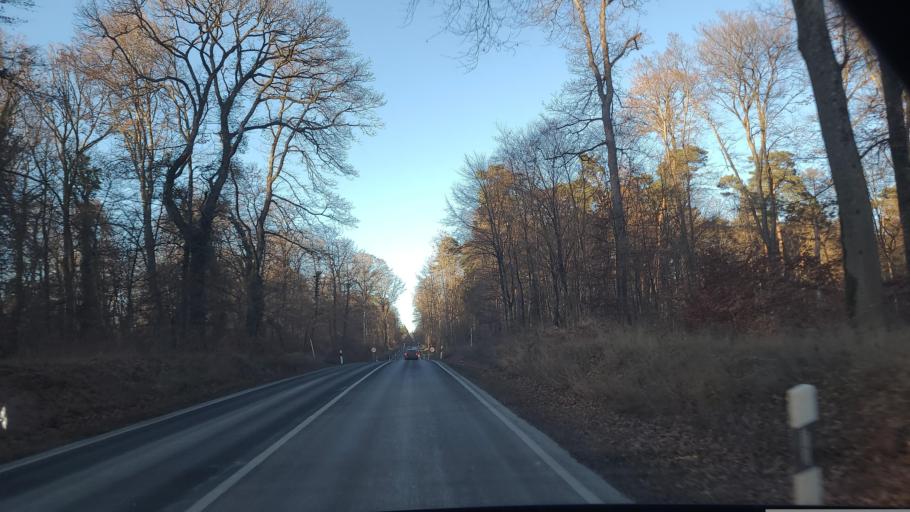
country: LU
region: Luxembourg
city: Bridel
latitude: 49.6410
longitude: 6.0871
